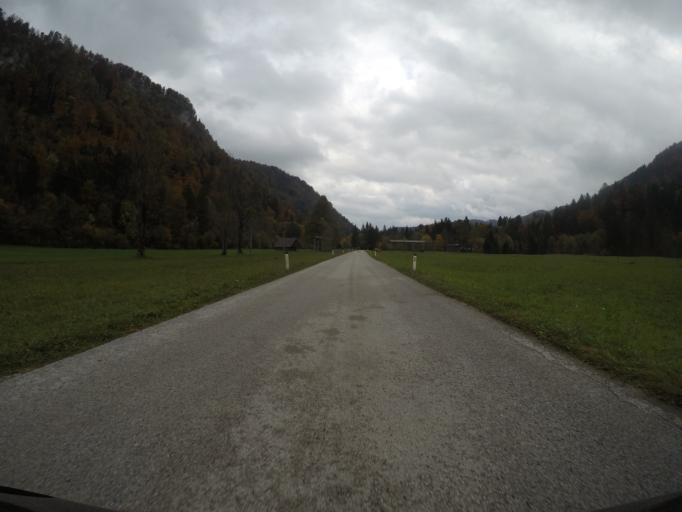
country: SI
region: Gorje
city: Zgornje Gorje
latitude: 46.3836
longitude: 14.0423
